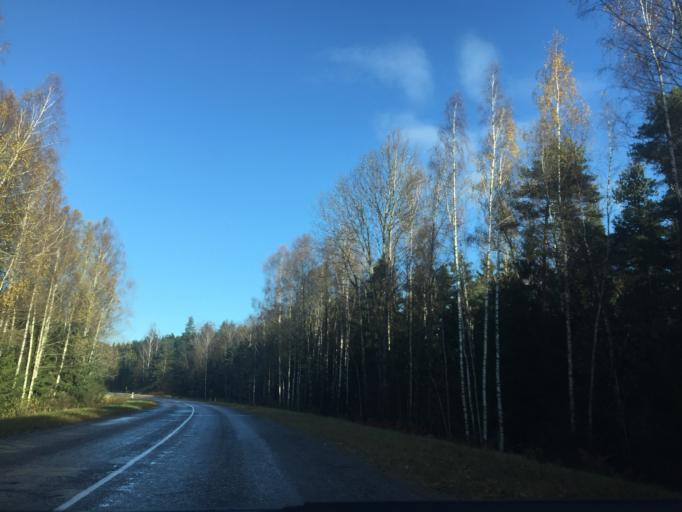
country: LV
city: Tireli
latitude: 56.8899
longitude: 23.5388
